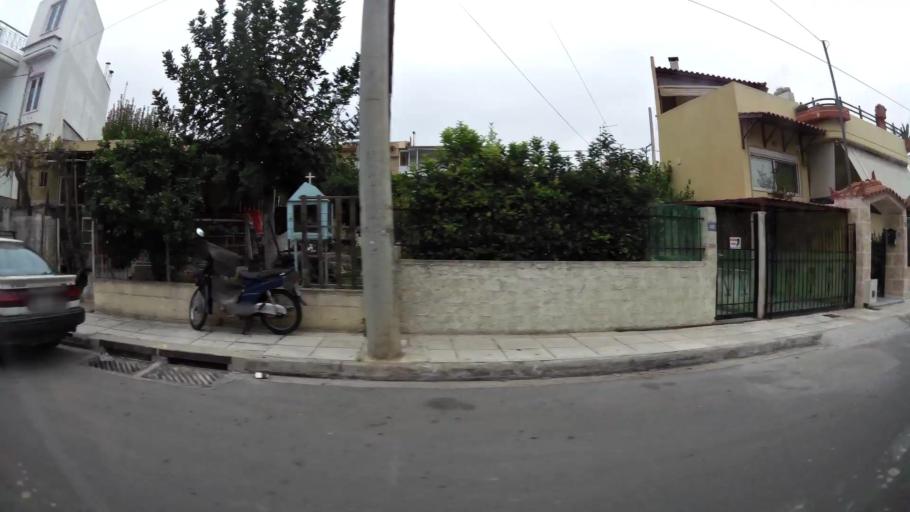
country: GR
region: Attica
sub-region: Nomarchia Athinas
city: Ilion
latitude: 38.0385
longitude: 23.7112
